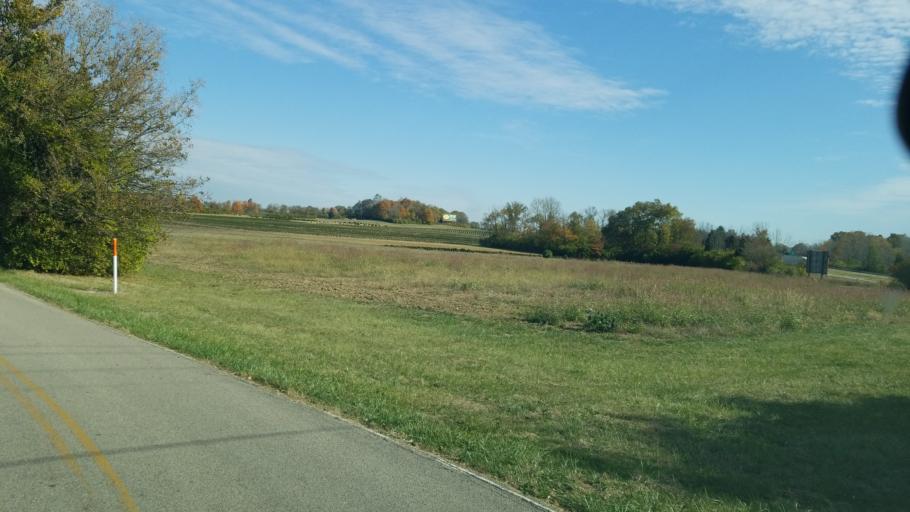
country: US
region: Ohio
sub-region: Warren County
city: Lebanon
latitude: 39.4101
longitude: -84.1703
